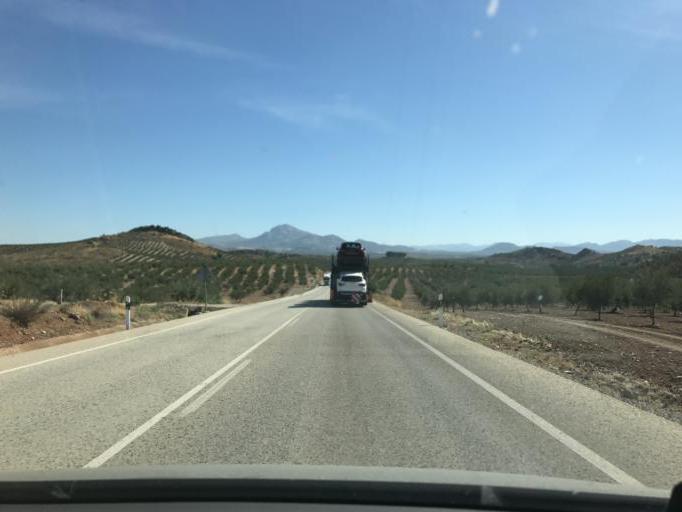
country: ES
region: Andalusia
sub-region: Province of Cordoba
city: Fuente-Tojar
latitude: 37.5613
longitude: -4.1968
